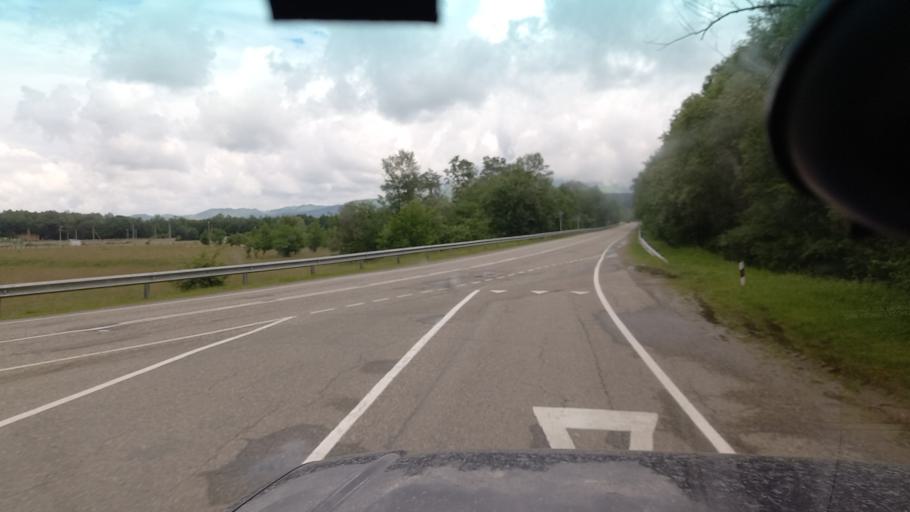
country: RU
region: Krasnodarskiy
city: Psebay
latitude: 44.0883
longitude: 40.7861
